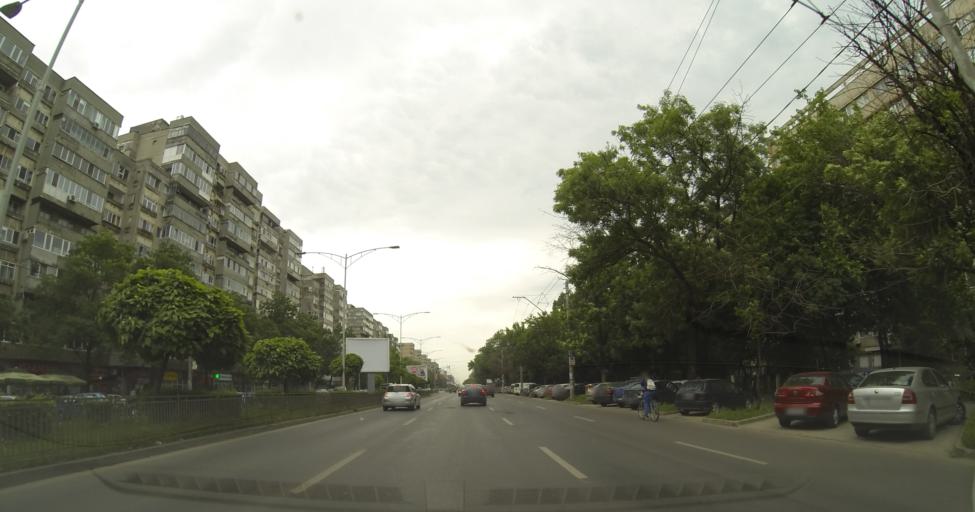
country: RO
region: Ilfov
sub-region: Comuna Chiajna
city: Rosu
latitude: 44.4343
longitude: 26.0270
